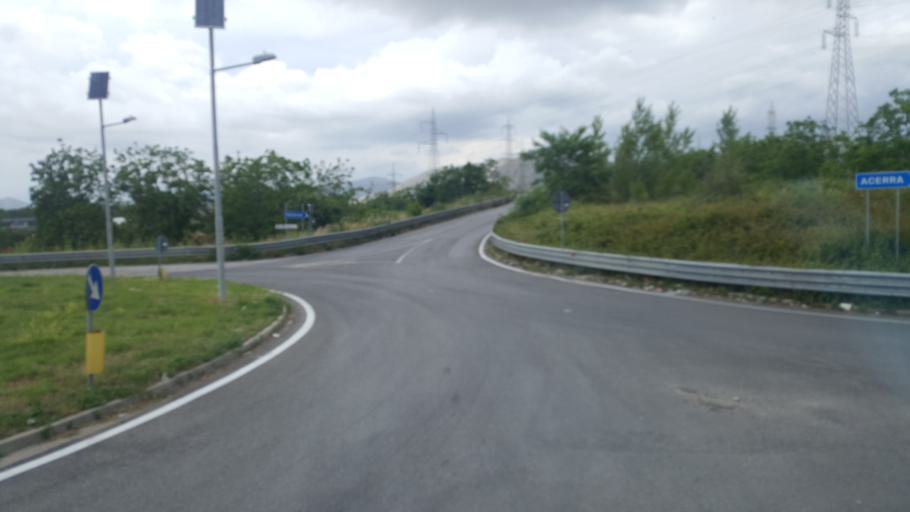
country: IT
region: Campania
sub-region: Provincia di Caserta
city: Maddaloni
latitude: 41.0140
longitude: 14.3711
